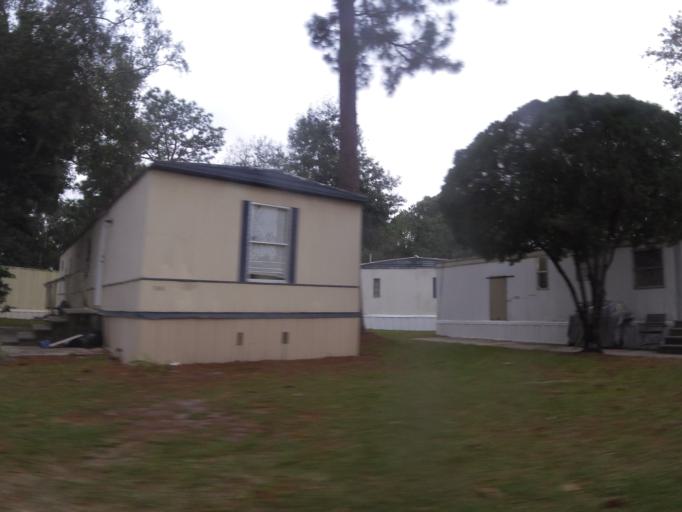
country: US
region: Florida
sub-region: Clay County
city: Bellair-Meadowbrook Terrace
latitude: 30.2471
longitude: -81.8269
